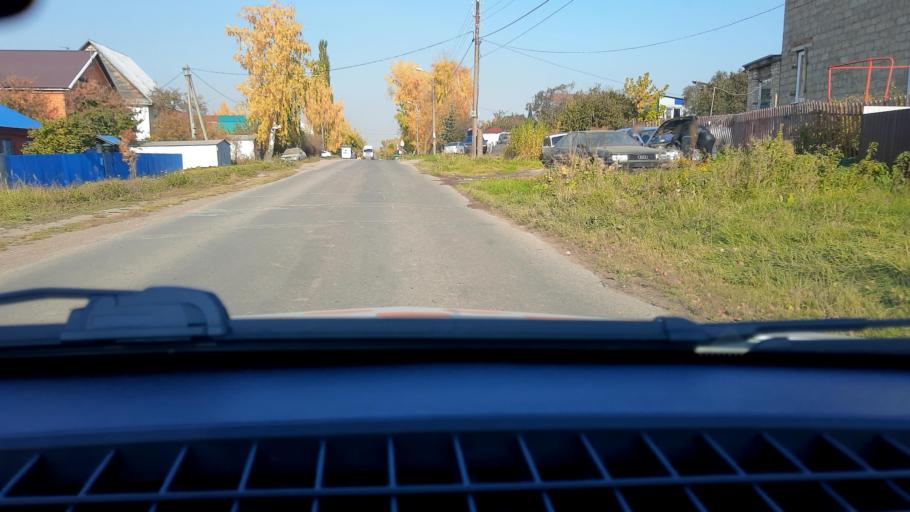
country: RU
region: Bashkortostan
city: Ufa
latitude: 54.8362
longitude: 56.1444
